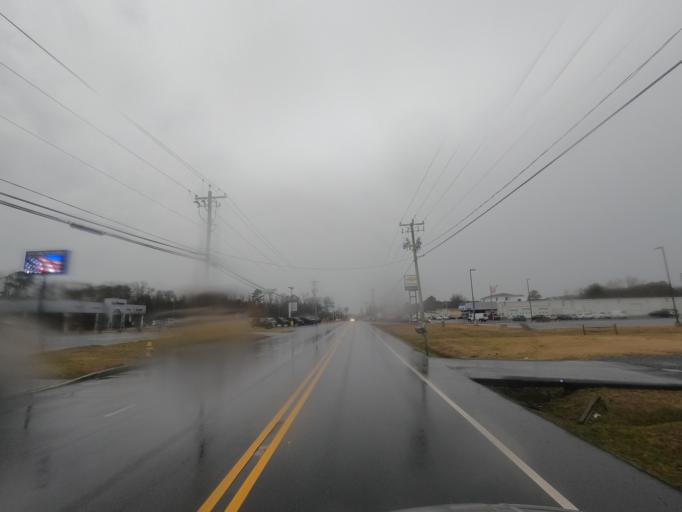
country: US
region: Maryland
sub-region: Worcester County
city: Berlin
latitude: 38.3400
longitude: -75.2005
